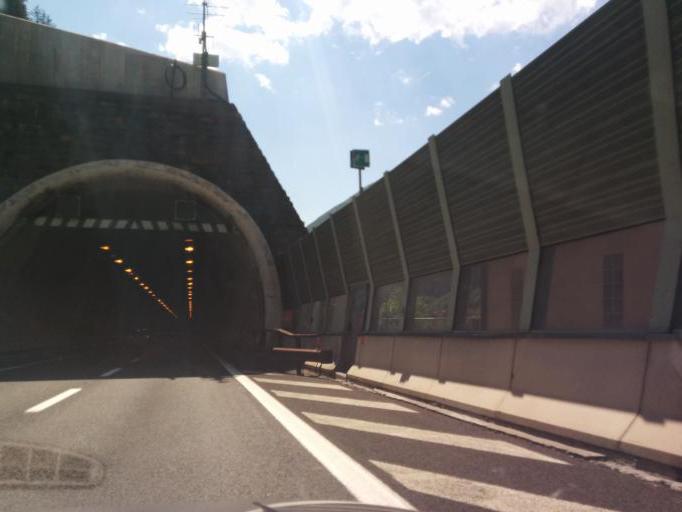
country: IT
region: Trentino-Alto Adige
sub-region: Bolzano
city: Fortezza
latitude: 46.7926
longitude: 11.6100
